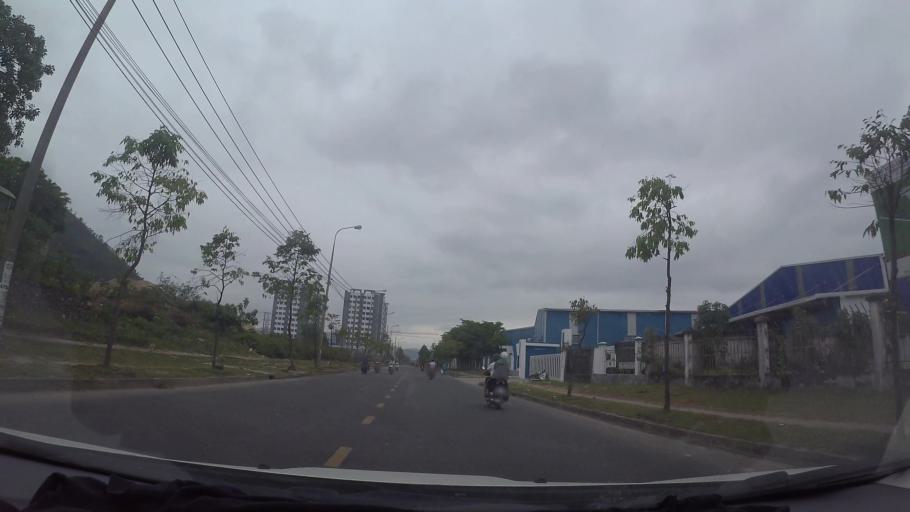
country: VN
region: Da Nang
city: Lien Chieu
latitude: 16.0734
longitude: 108.1382
